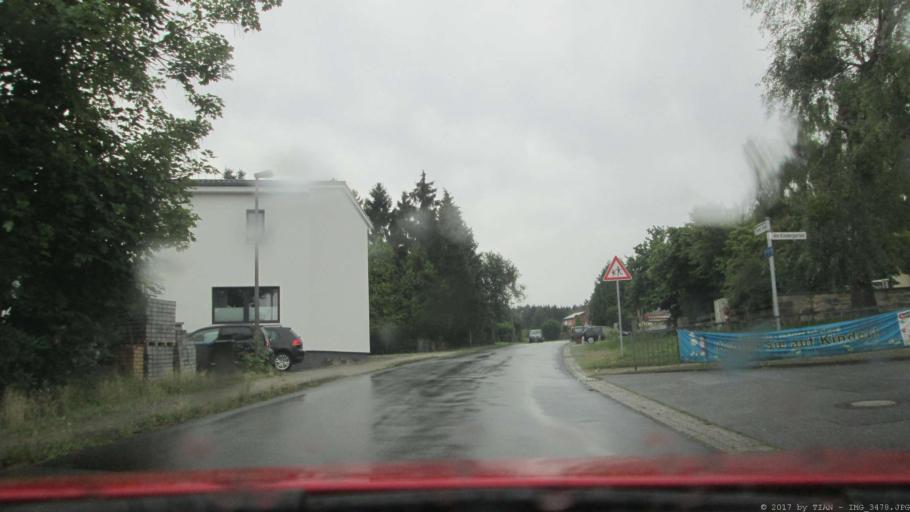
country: DE
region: Lower Saxony
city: Gross Twulpstedt
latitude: 52.3878
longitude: 10.8529
